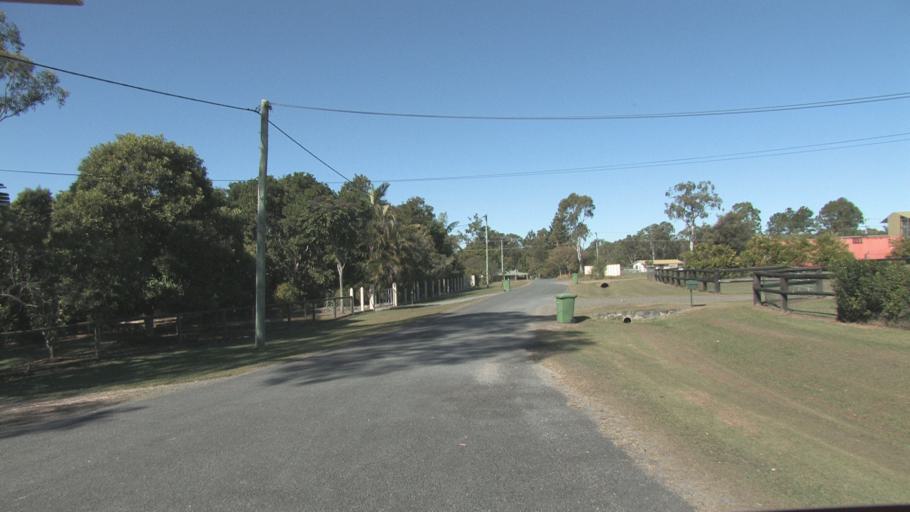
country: AU
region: Queensland
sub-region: Logan
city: Park Ridge South
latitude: -27.7226
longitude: 153.0535
